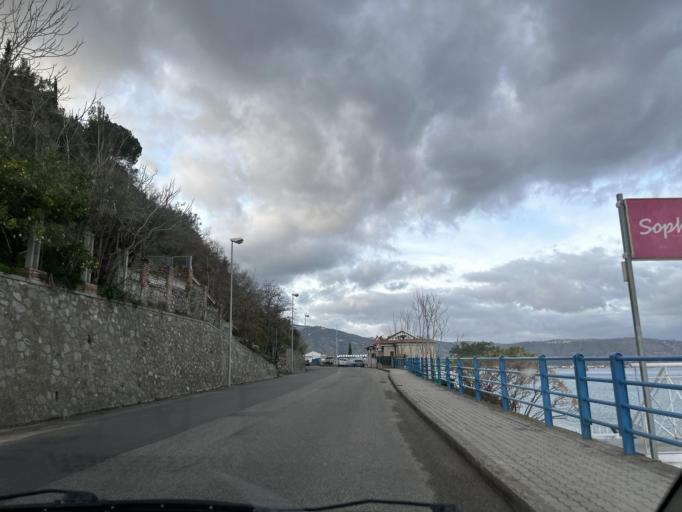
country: IT
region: Calabria
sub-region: Provincia di Catanzaro
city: Soverato Marina
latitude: 38.6933
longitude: 16.5451
